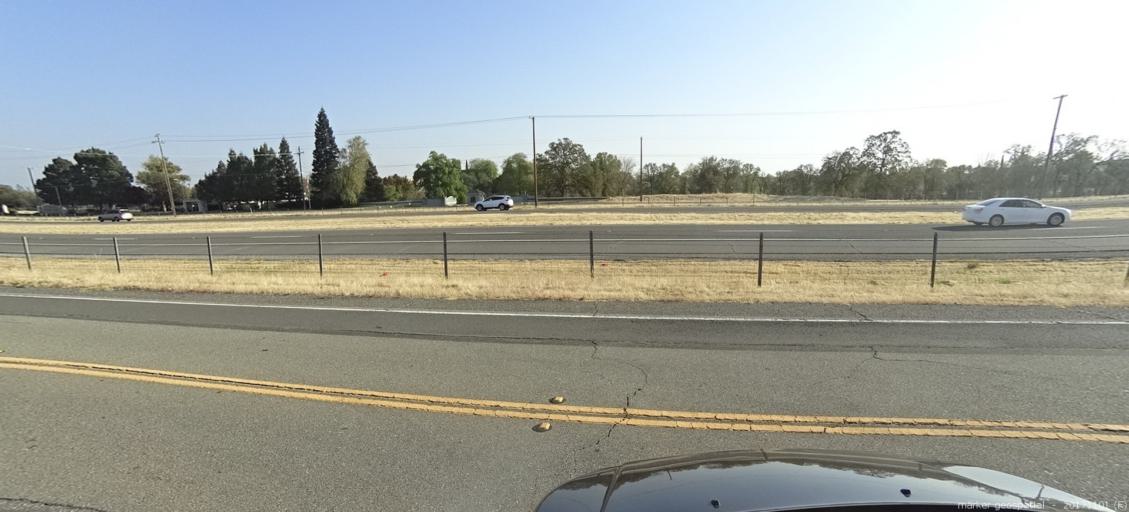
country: US
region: California
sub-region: Shasta County
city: Redding
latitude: 40.6185
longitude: -122.3312
